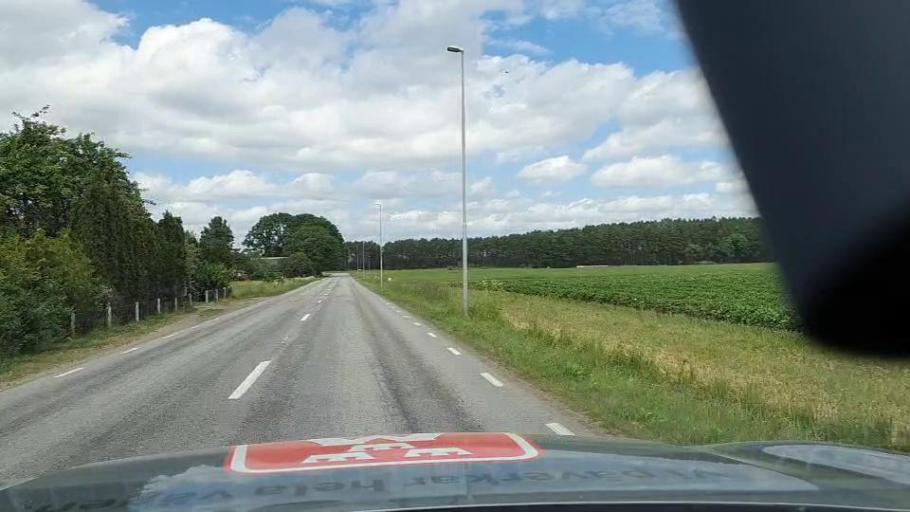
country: SE
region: Blekinge
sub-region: Karlshamns Kommun
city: Morrum
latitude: 56.0864
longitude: 14.7047
